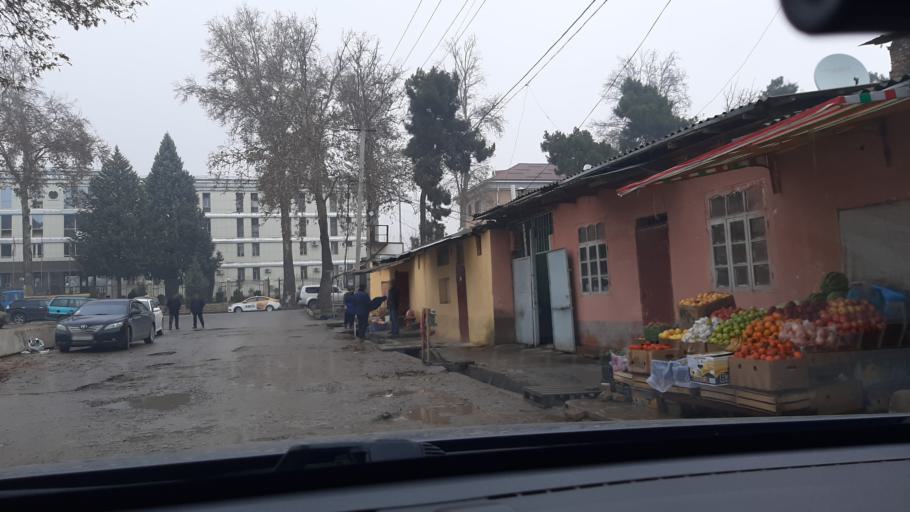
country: TJ
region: Dushanbe
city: Dushanbe
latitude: 38.5672
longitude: 68.8024
